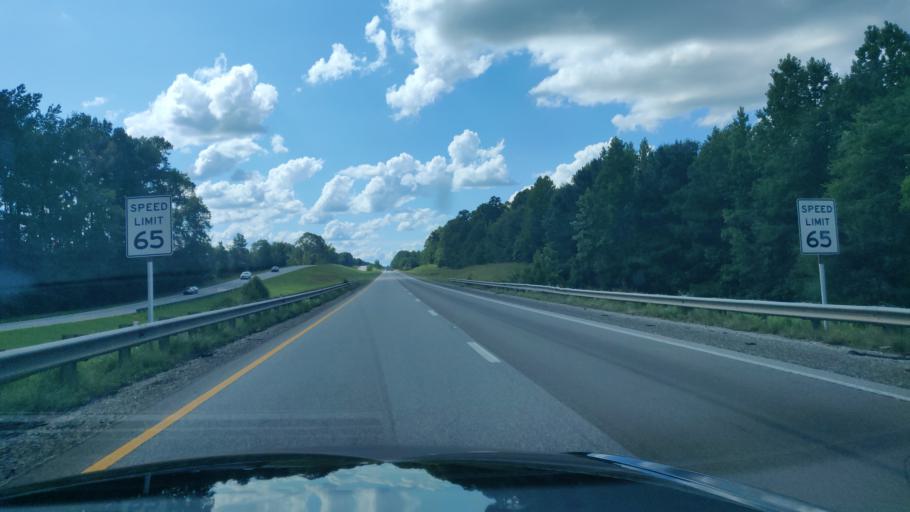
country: US
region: Alabama
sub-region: Lee County
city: Opelika
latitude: 32.6051
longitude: -85.2495
